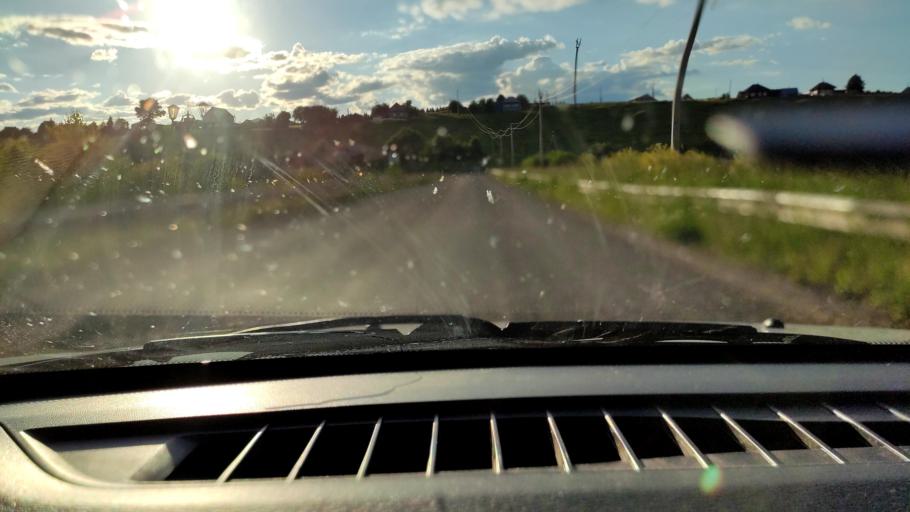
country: RU
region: Perm
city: Uinskoye
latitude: 57.1186
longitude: 56.5222
